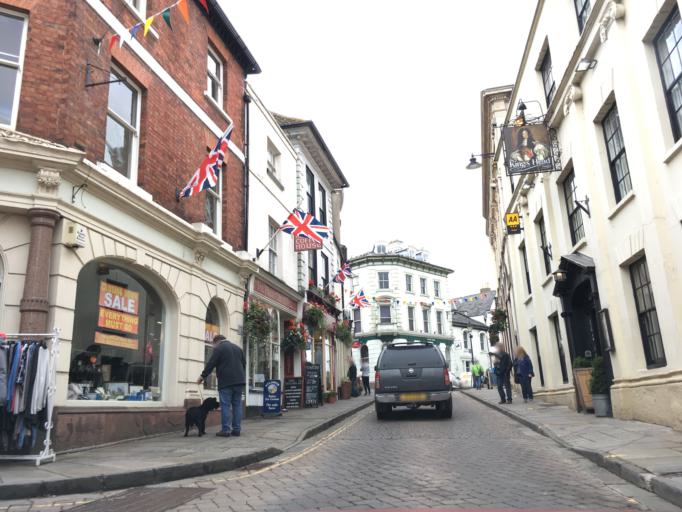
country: GB
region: England
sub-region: Herefordshire
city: Ross on Wye
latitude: 51.9143
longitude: -2.5847
